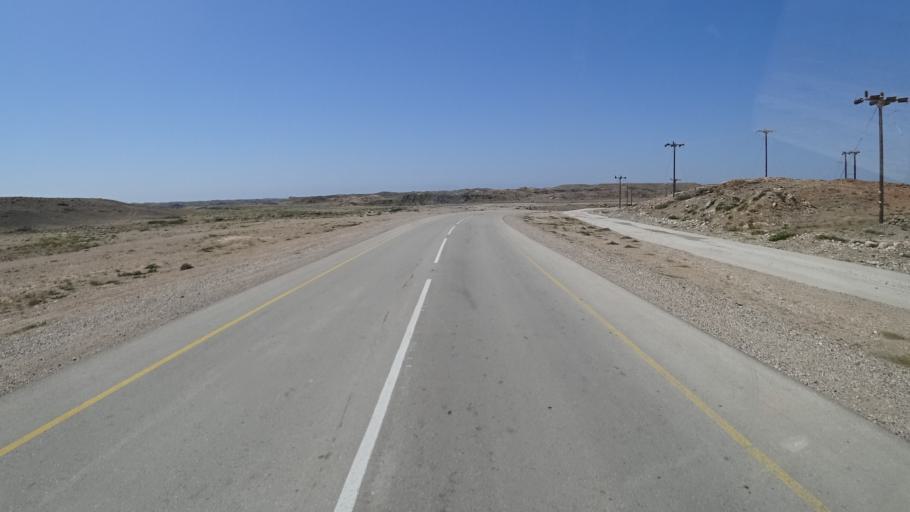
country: OM
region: Zufar
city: Salalah
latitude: 17.0270
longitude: 54.8006
